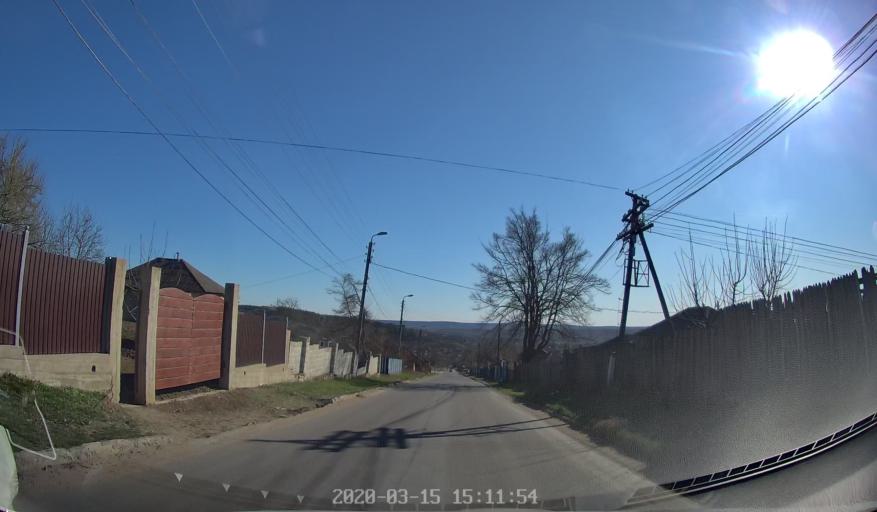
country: MD
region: Orhei
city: Orhei
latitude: 47.2599
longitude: 28.7747
